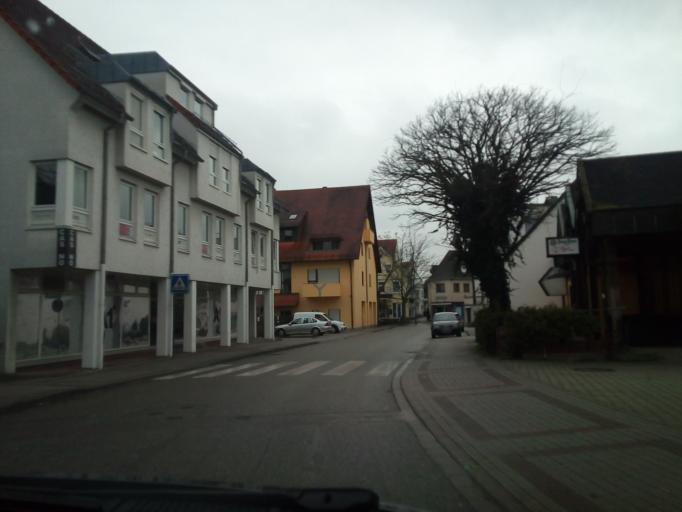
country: DE
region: Baden-Wuerttemberg
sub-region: Karlsruhe Region
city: Buhl
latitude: 48.6954
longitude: 8.1392
